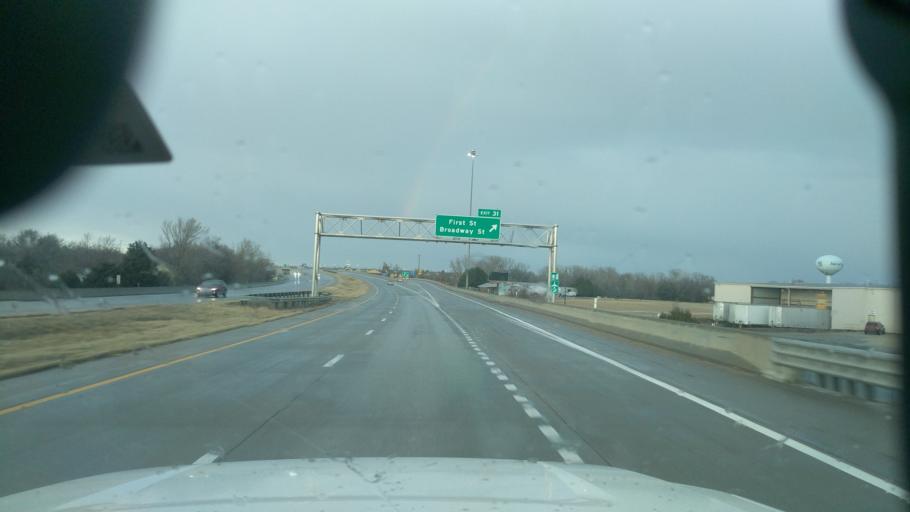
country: US
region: Kansas
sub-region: Harvey County
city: Newton
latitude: 38.0373
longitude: -97.3231
